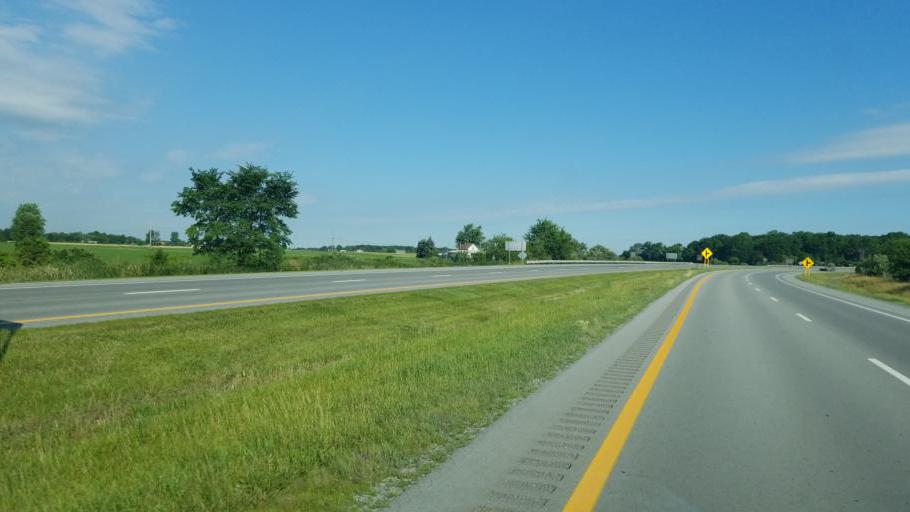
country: US
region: Ohio
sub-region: Hancock County
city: Findlay
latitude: 40.9995
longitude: -83.6569
